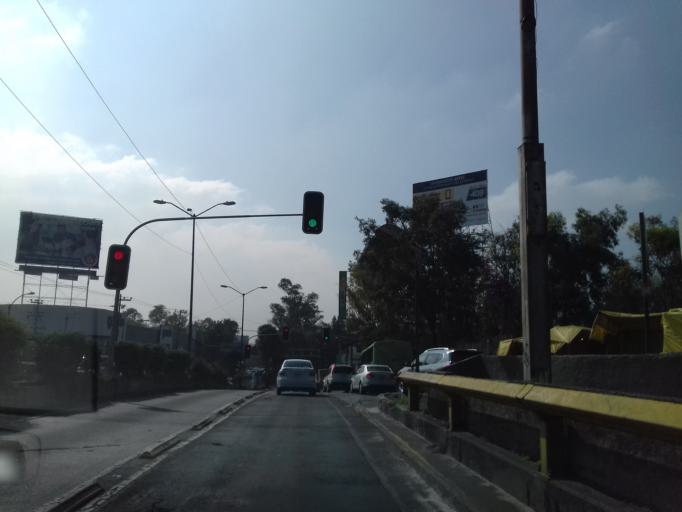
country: MX
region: Mexico City
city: Polanco
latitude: 19.4026
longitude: -99.1871
